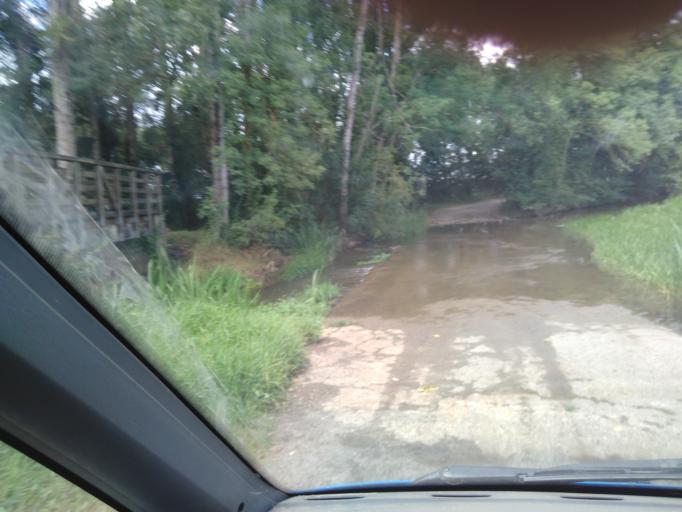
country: FR
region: Pays de la Loire
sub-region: Departement de la Vendee
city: Sainte-Hermine
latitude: 46.5573
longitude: -1.0277
